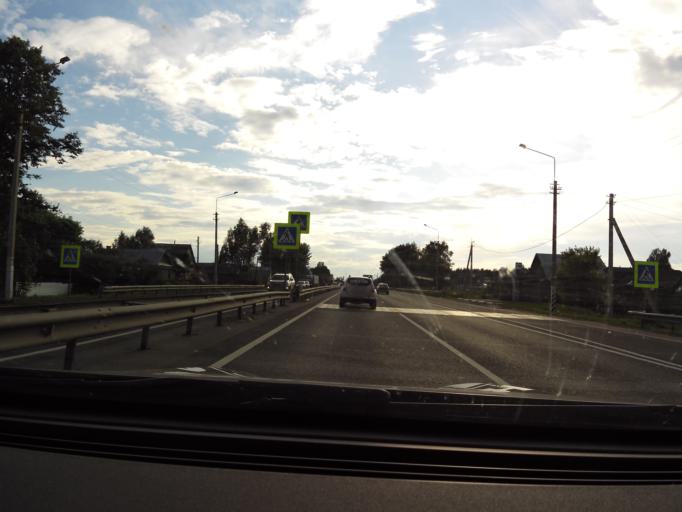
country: RU
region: Vladimir
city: Novki
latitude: 56.2017
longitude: 41.1030
